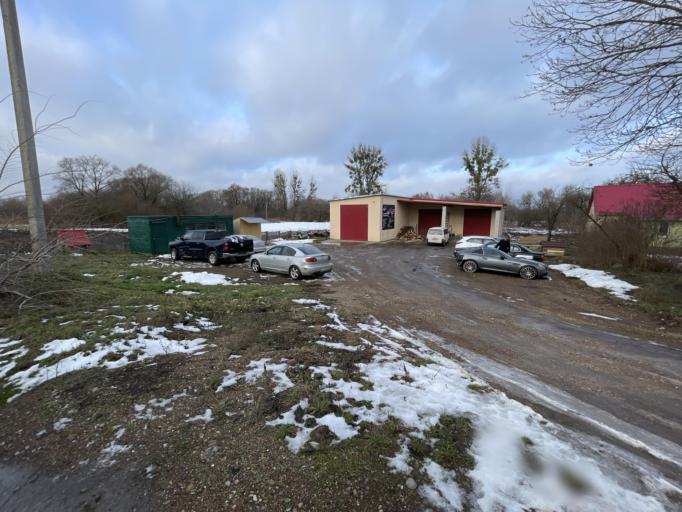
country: BY
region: Grodnenskaya
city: Hrodna
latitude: 53.6922
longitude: 23.9018
